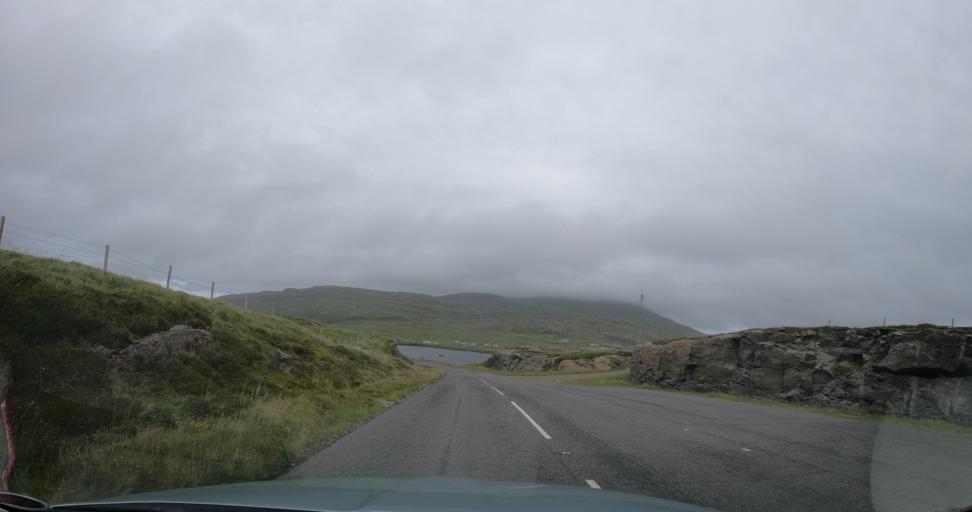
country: GB
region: Scotland
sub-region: Eilean Siar
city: Barra
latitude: 56.9504
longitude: -7.5105
